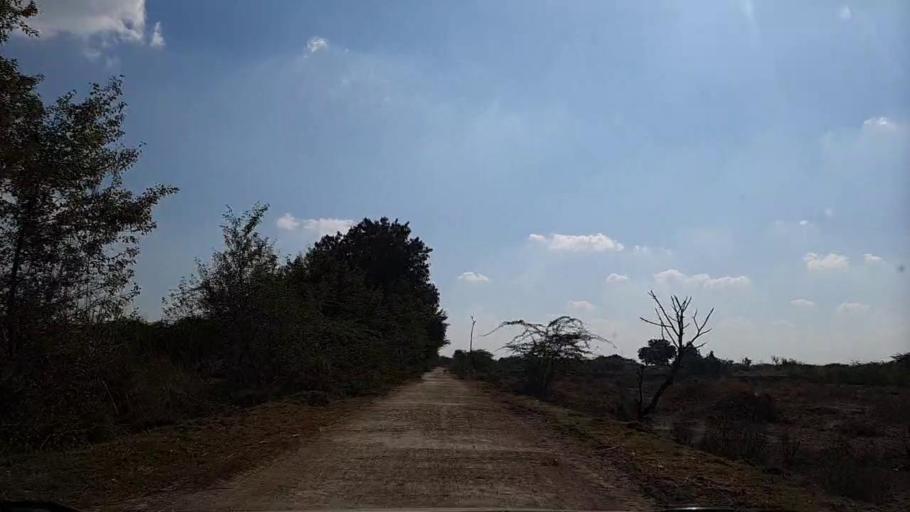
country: PK
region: Sindh
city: Pithoro
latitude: 25.6430
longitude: 69.4475
